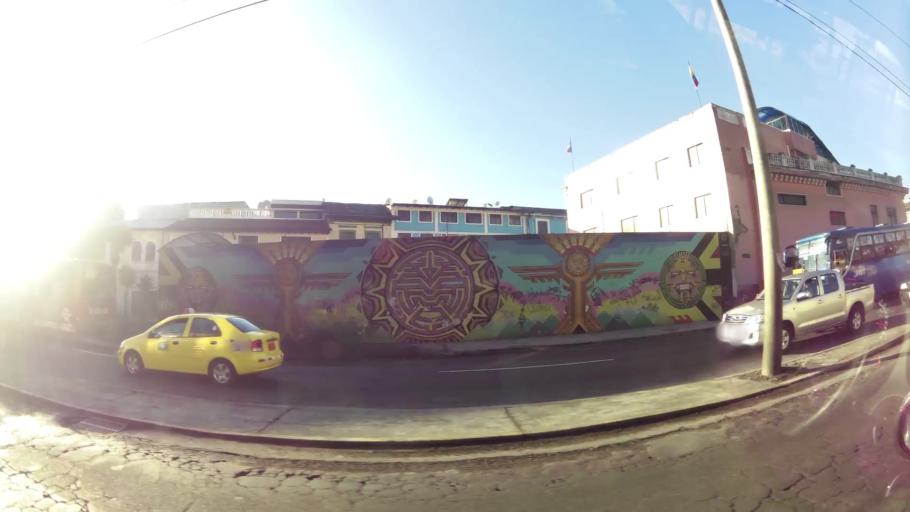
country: EC
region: Pichincha
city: Quito
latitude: -0.2186
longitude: -78.5063
